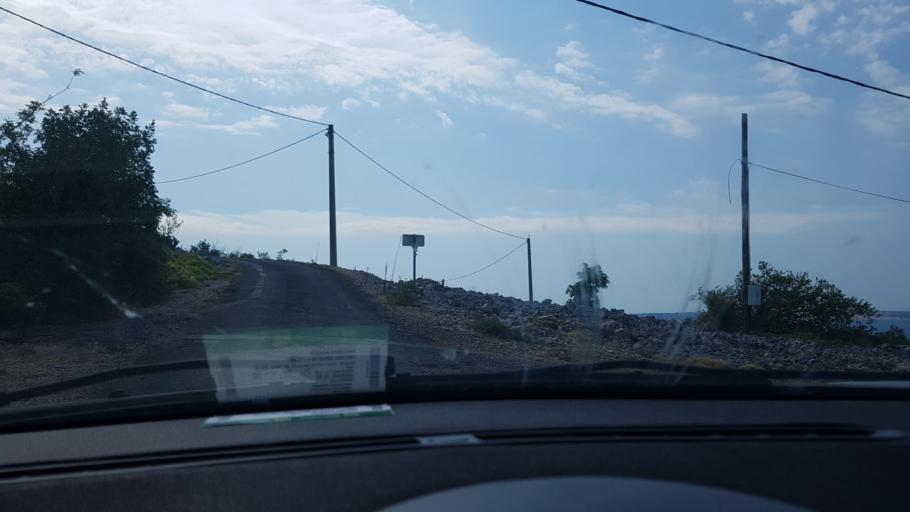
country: HR
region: Primorsko-Goranska
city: Banjol
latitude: 44.6968
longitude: 14.9083
